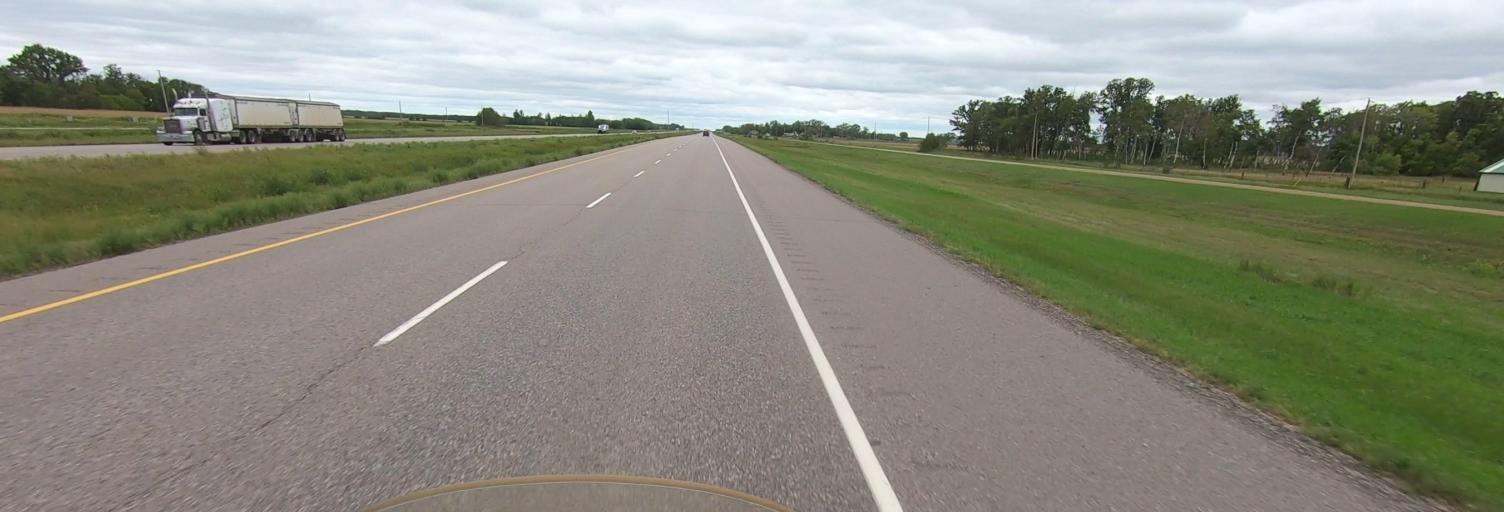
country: CA
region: Manitoba
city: Portage la Prairie
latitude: 49.9751
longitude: -98.5674
